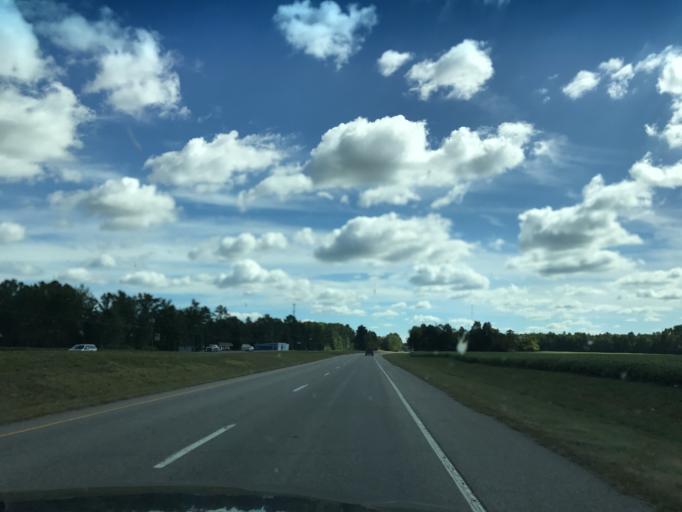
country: US
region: Virginia
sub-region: Middlesex County
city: Saluda
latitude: 37.7012
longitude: -76.6878
